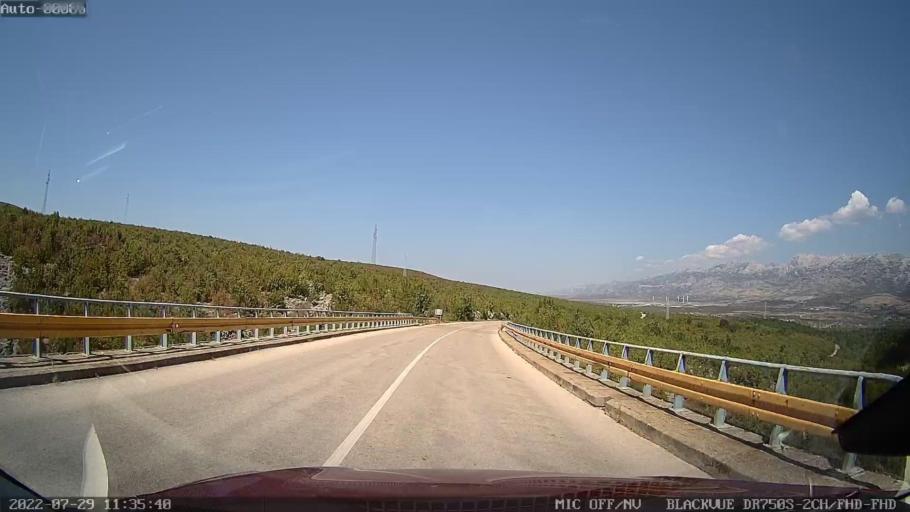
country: HR
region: Zadarska
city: Obrovac
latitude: 44.1833
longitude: 15.7080
